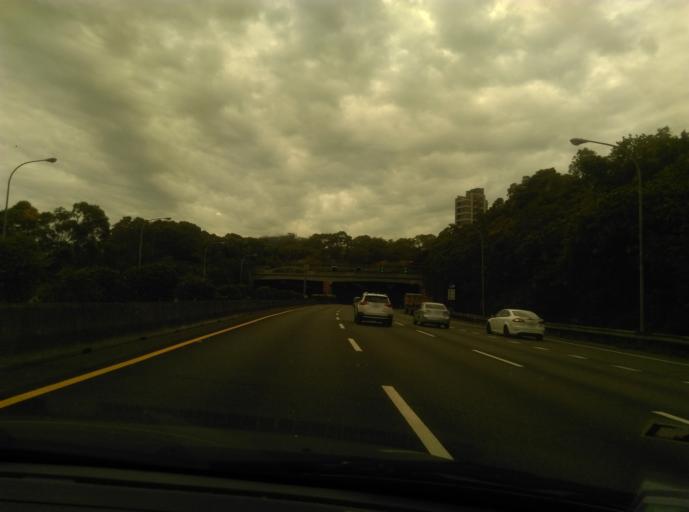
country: TW
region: Taiwan
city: Daxi
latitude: 24.9094
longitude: 121.2893
